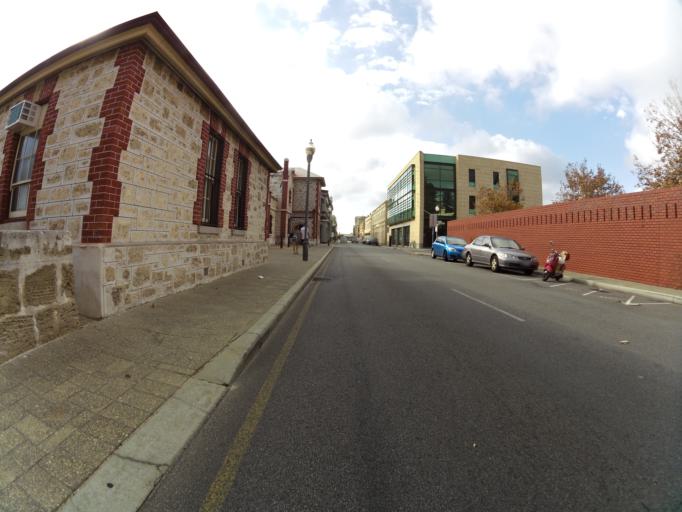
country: AU
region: Western Australia
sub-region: Fremantle
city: South Fremantle
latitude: -32.0573
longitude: 115.7431
